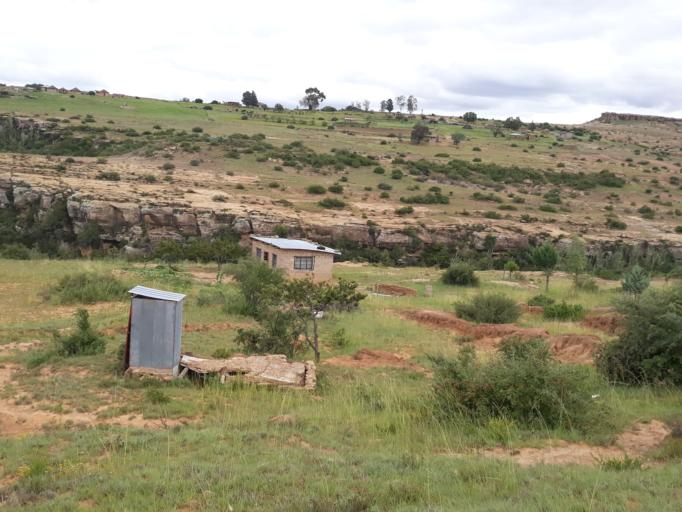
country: LS
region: Quthing
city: Quthing
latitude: -30.3328
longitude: 27.5296
